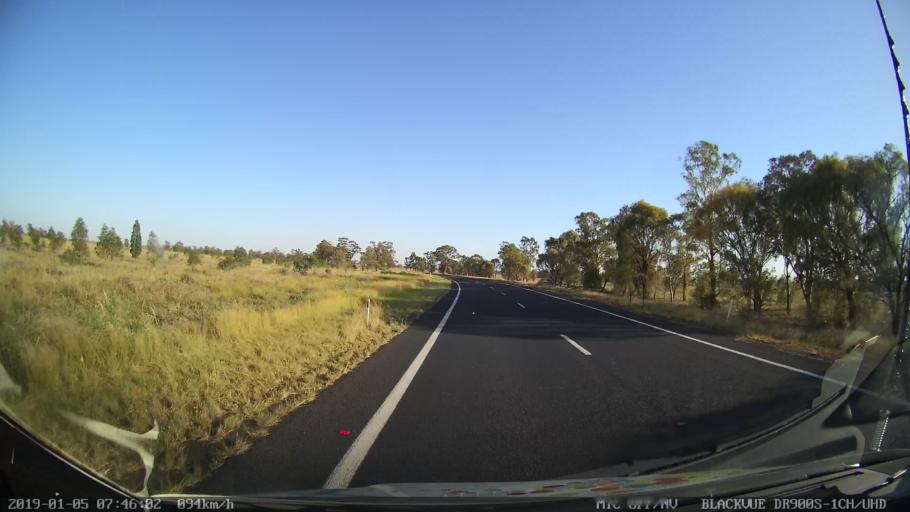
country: AU
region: New South Wales
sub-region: Gilgandra
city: Gilgandra
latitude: -31.8501
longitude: 148.6444
